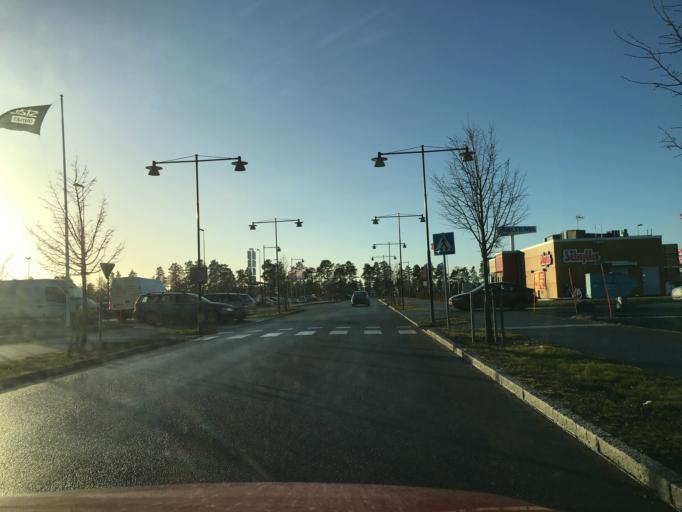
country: SE
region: Kalmar
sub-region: Vasterviks Kommun
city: Vaestervik
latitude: 57.7691
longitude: 16.5962
